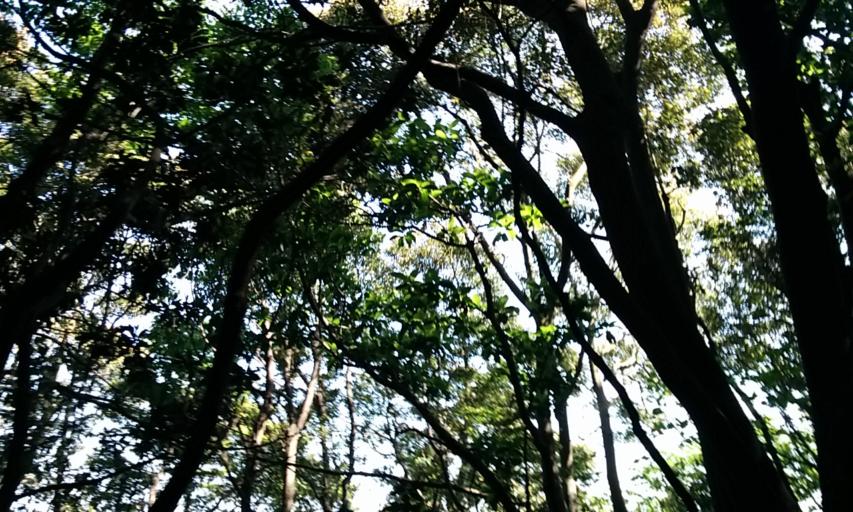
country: JP
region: Oita
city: Usuki
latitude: 33.3468
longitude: 132.0190
